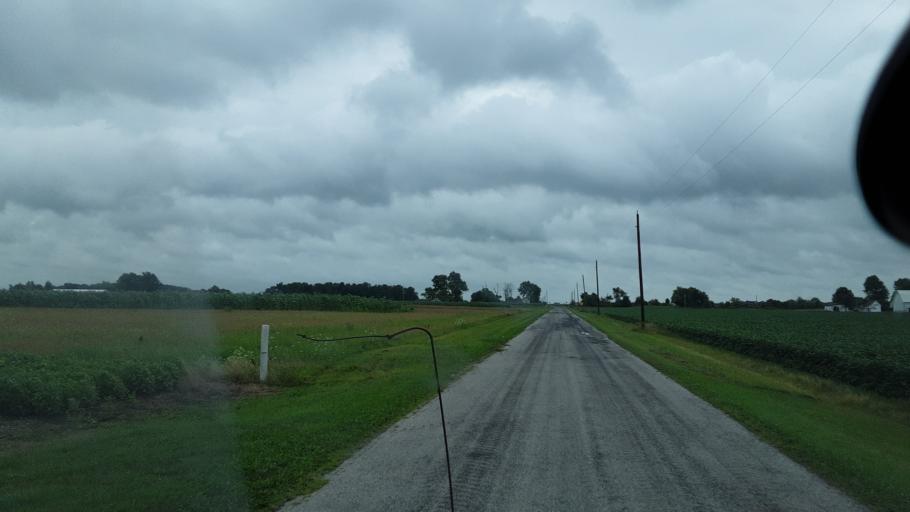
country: US
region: Indiana
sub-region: Wells County
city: Bluffton
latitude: 40.7903
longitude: -85.0717
